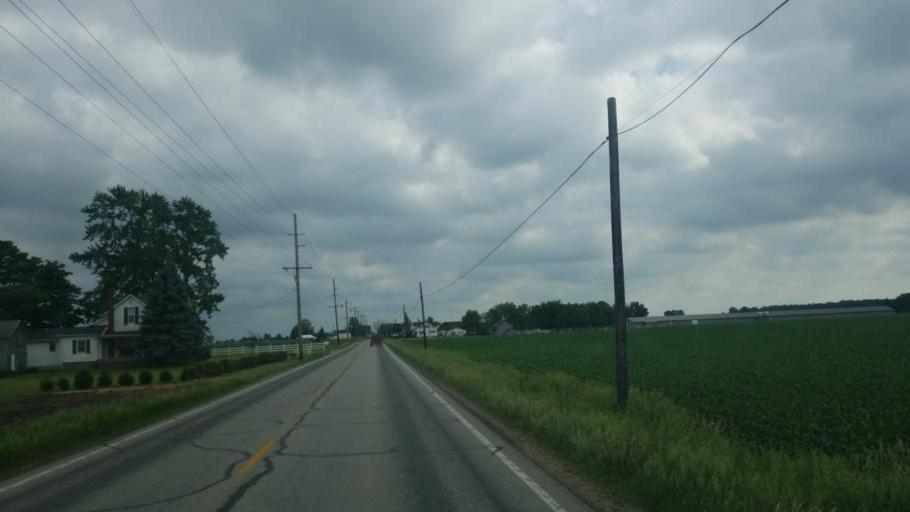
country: US
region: Indiana
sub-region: Elkhart County
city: Nappanee
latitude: 41.3716
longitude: -86.0007
